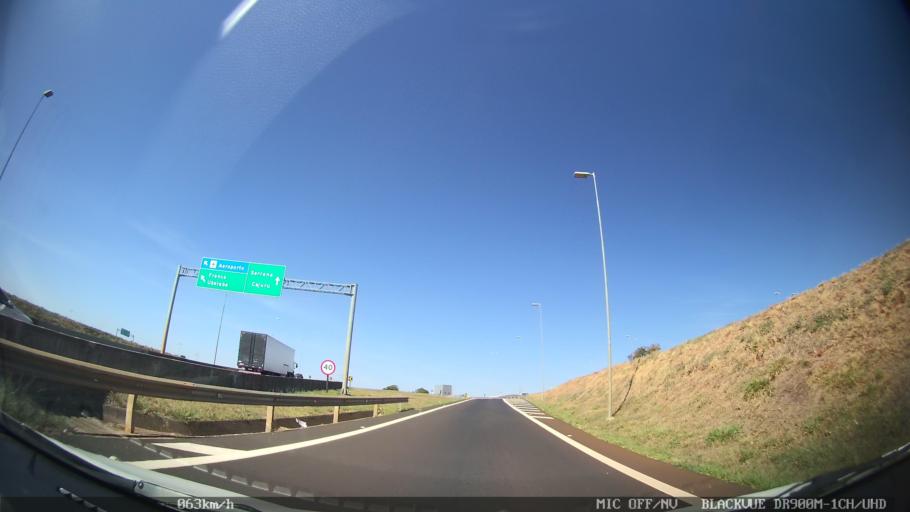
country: BR
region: Sao Paulo
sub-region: Ribeirao Preto
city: Ribeirao Preto
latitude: -21.2073
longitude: -47.7595
